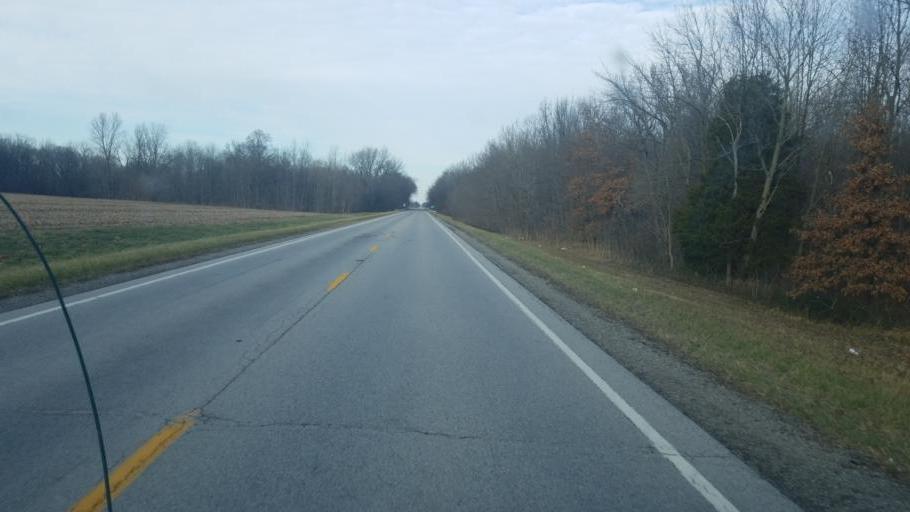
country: US
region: Illinois
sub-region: Lawrence County
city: Bridgeport
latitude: 38.5646
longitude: -87.6947
